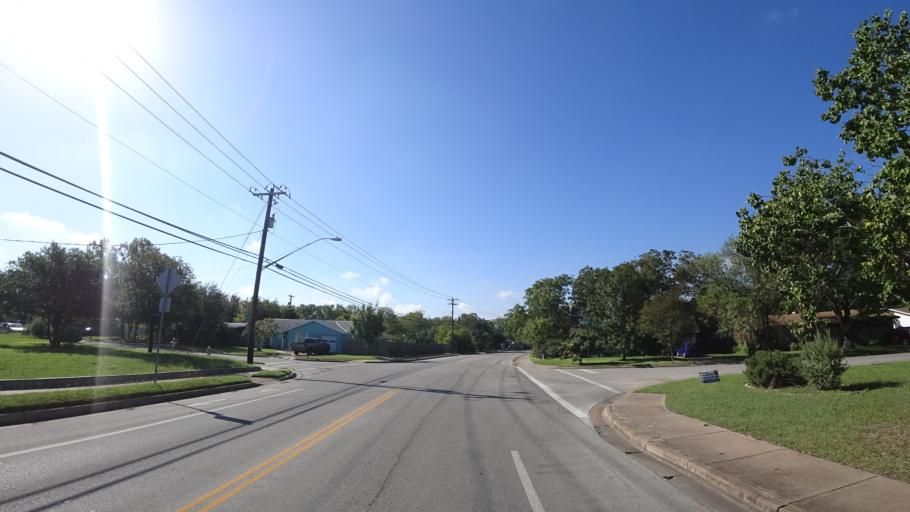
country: US
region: Texas
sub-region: Travis County
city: Austin
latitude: 30.3412
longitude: -97.7125
